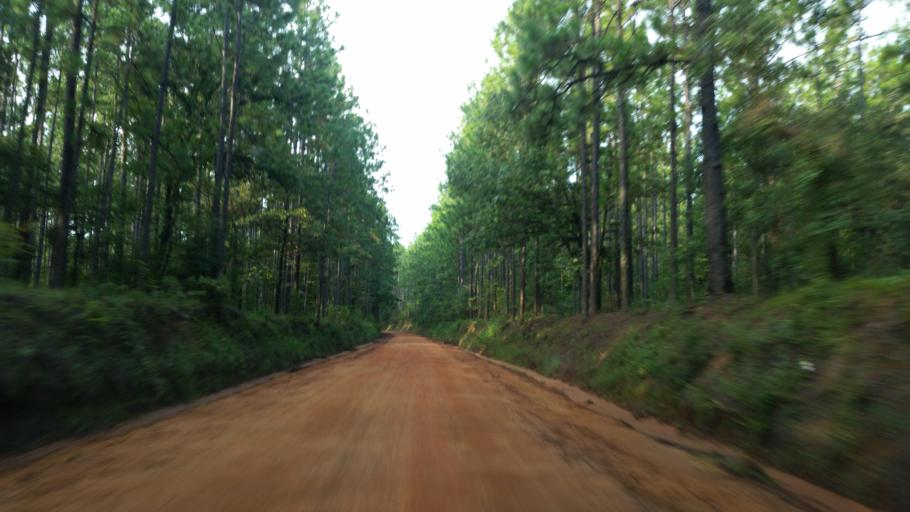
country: US
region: Alabama
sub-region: Escambia County
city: Atmore
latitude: 30.9528
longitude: -87.5722
